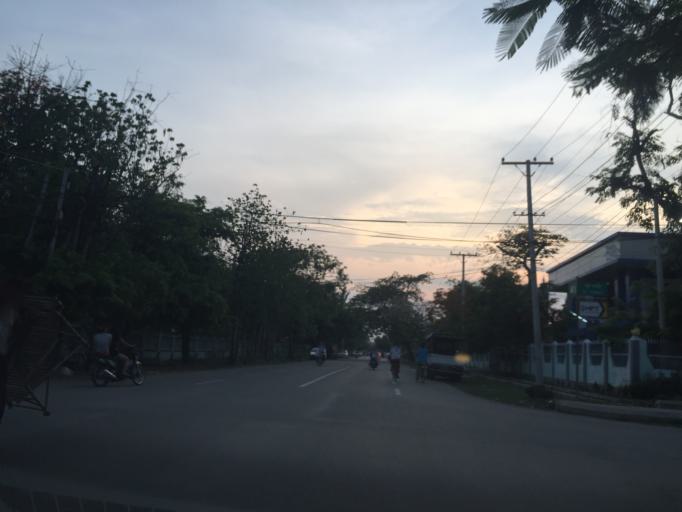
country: MM
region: Mandalay
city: Mandalay
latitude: 21.9792
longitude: 96.1008
